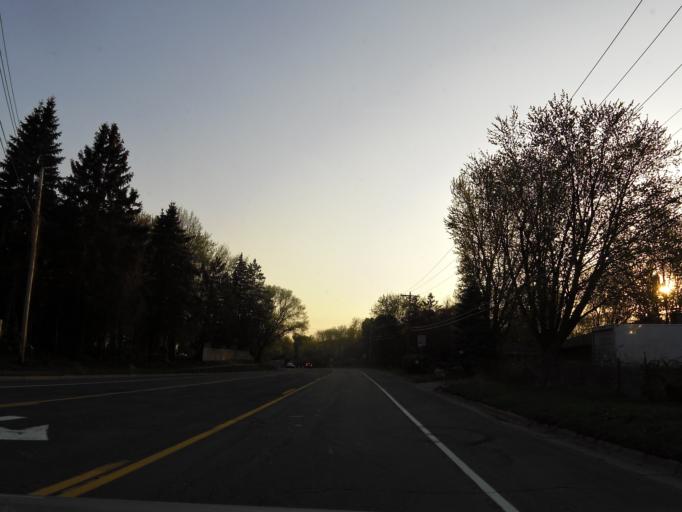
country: US
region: Minnesota
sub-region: Scott County
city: Savage
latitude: 44.7700
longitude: -93.3152
